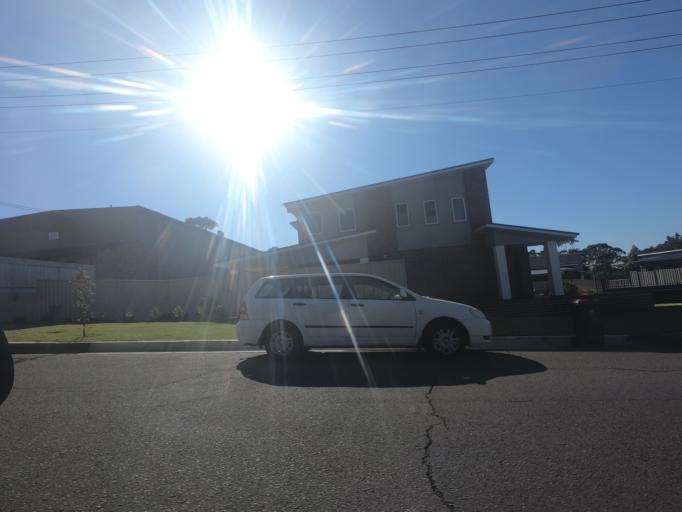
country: AU
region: New South Wales
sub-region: Wollongong
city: Corrimal
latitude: -34.3732
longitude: 150.8880
